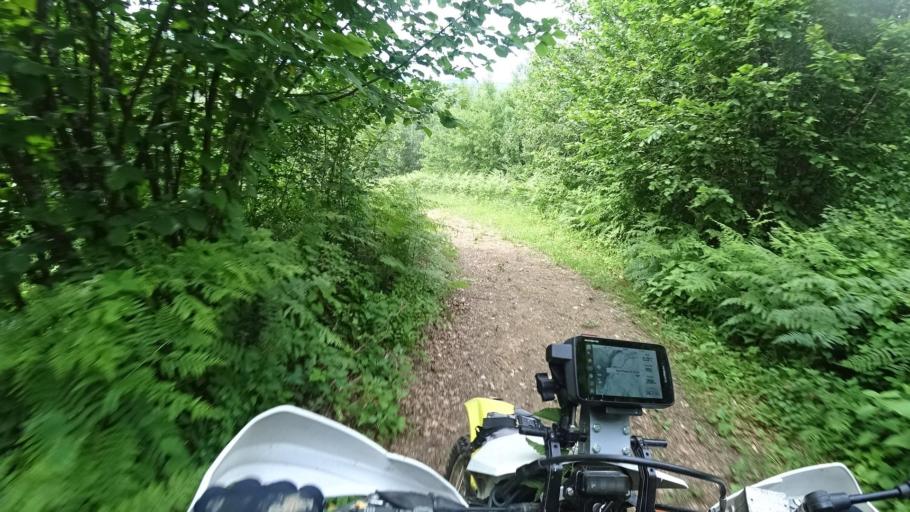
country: HR
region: Licko-Senjska
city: Jezerce
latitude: 44.9322
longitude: 15.6313
